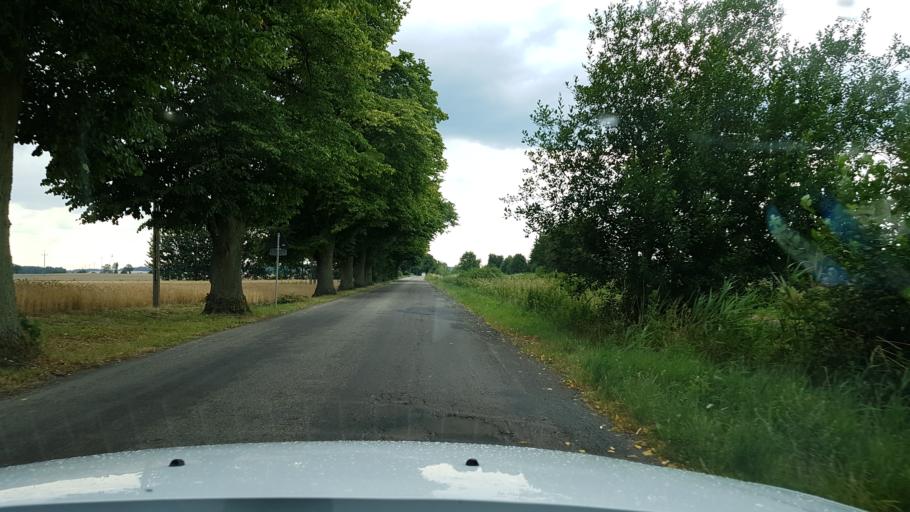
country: PL
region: West Pomeranian Voivodeship
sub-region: Powiat walecki
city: Walcz
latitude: 53.3505
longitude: 16.3609
